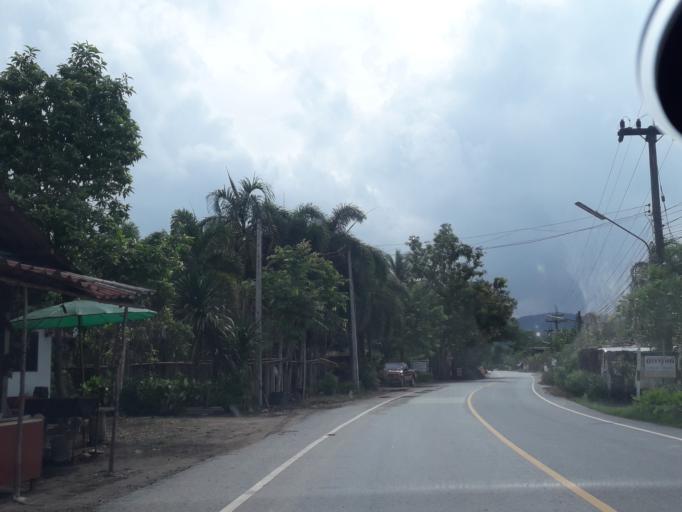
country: TH
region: Sara Buri
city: Wihan Daeng
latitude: 14.4076
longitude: 101.1070
